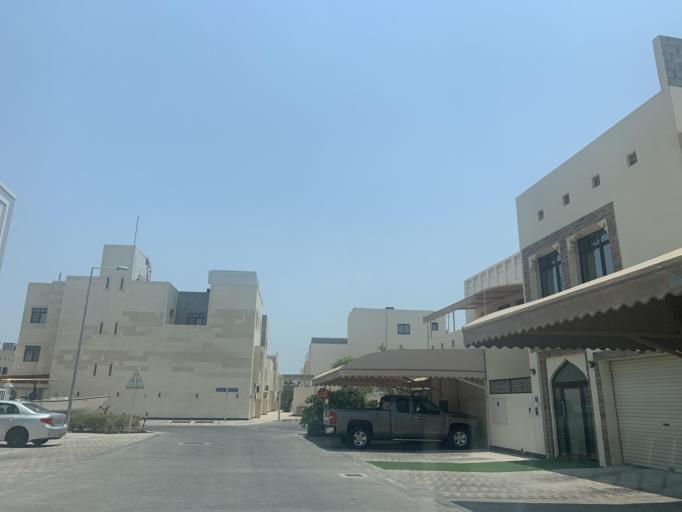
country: BH
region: Muharraq
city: Al Hadd
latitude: 26.2374
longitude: 50.6733
